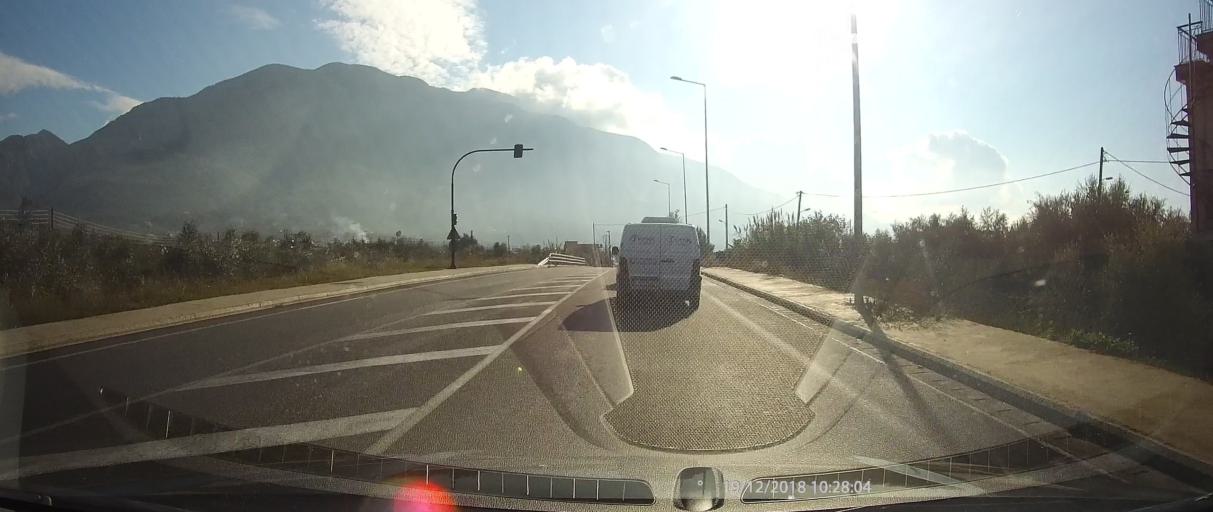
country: GR
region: Peloponnese
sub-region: Nomos Messinias
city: Kalamata
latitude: 37.0298
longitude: 22.1386
